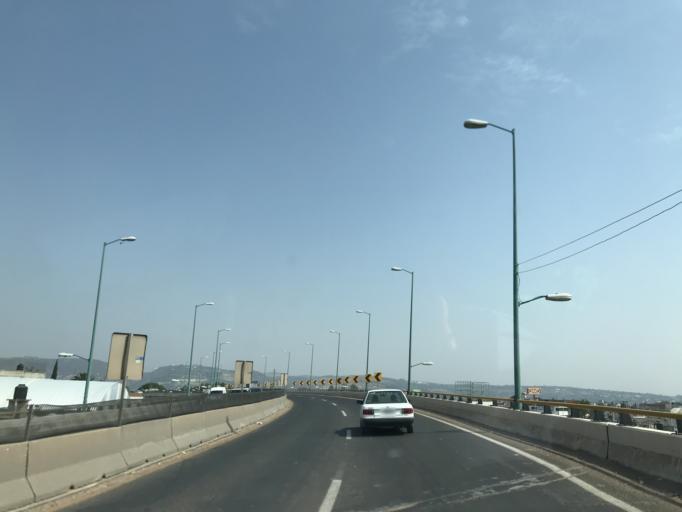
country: MX
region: Tlaxcala
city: Tlaxcala de Xicohtencatl
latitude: 19.3101
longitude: -98.2003
